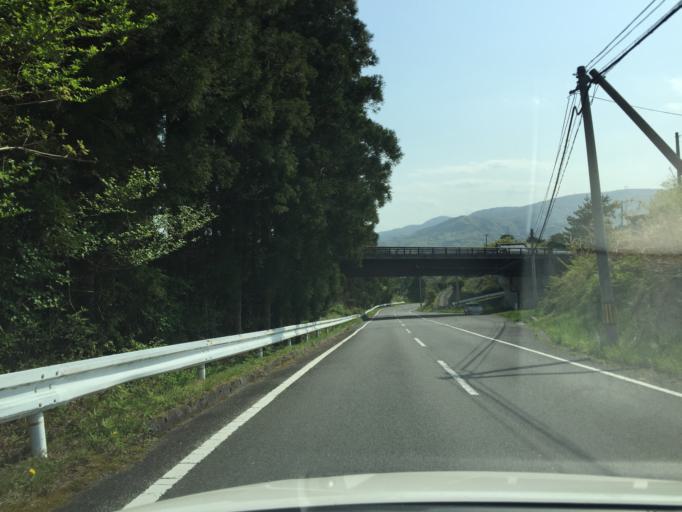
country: JP
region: Fukushima
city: Iwaki
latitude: 37.1487
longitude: 140.8583
